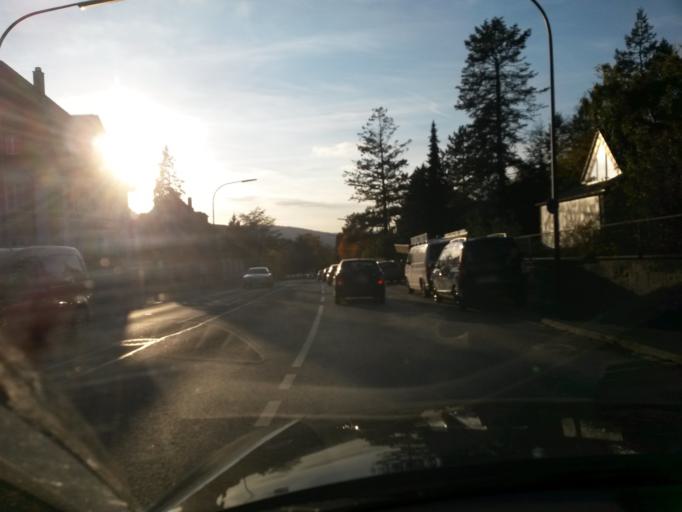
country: DE
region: Bavaria
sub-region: Regierungsbezirk Unterfranken
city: Wuerzburg
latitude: 49.7917
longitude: 9.9573
